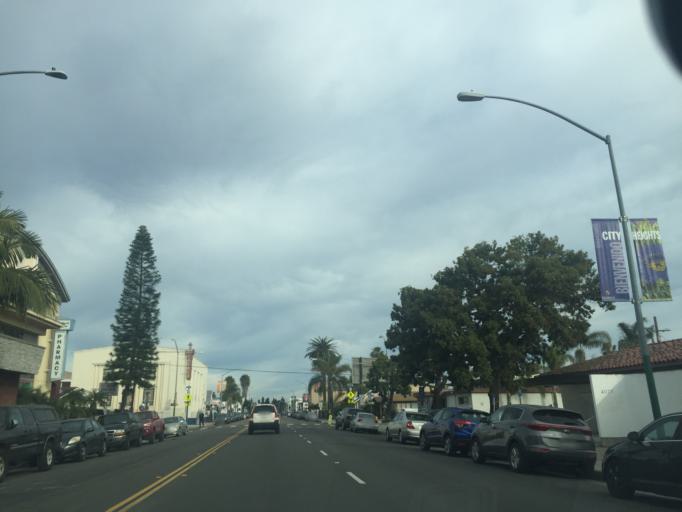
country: US
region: California
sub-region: San Diego County
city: San Diego
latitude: 32.7508
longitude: -117.1009
